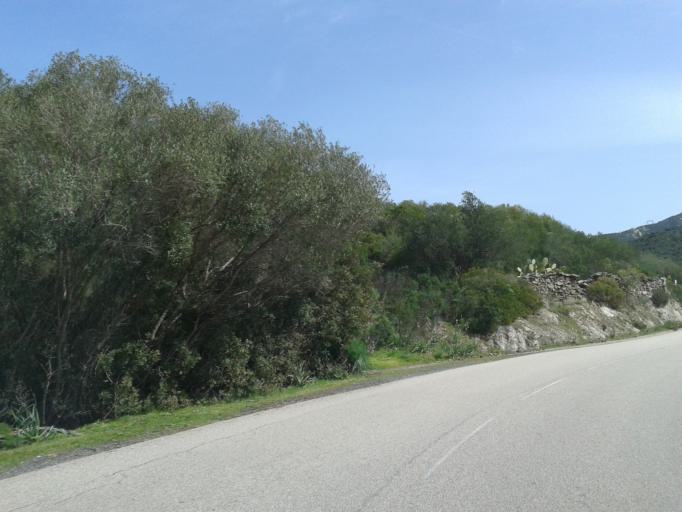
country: FR
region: Corsica
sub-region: Departement de la Haute-Corse
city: Monticello
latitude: 42.6484
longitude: 9.1043
